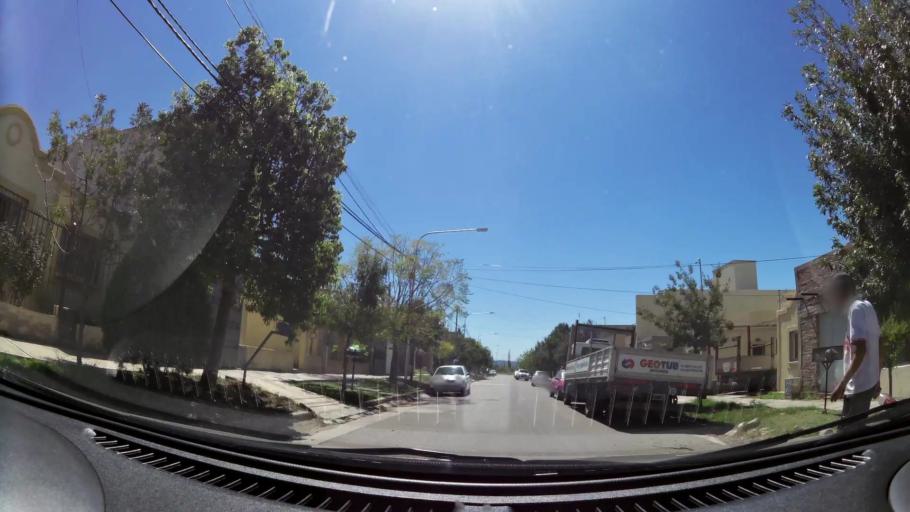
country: AR
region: Mendoza
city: Las Heras
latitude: -32.8482
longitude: -68.8571
